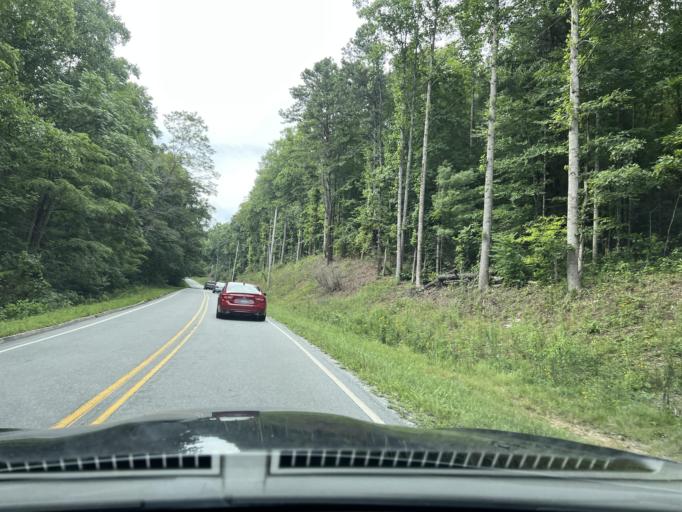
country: US
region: North Carolina
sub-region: Henderson County
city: Fruitland
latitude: 35.4144
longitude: -82.4101
